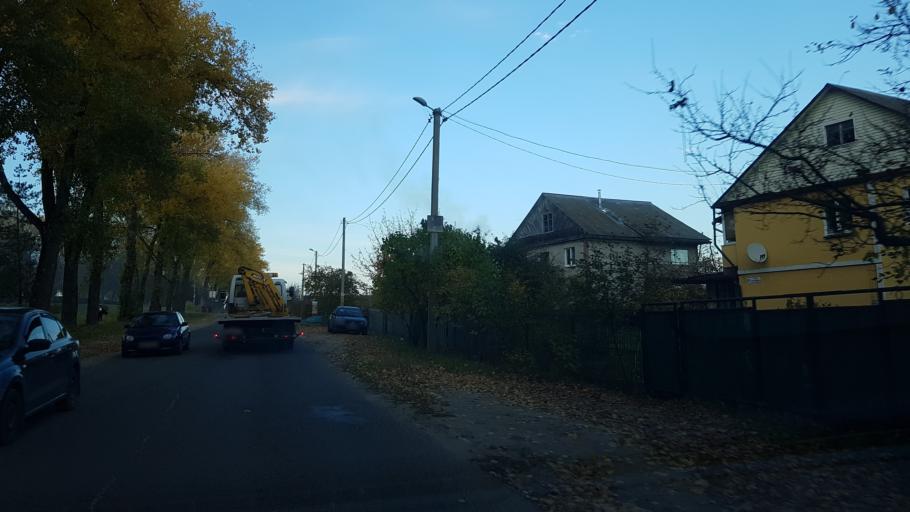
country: BY
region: Minsk
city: Vyaliki Trastsyanets
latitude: 53.8503
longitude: 27.7064
